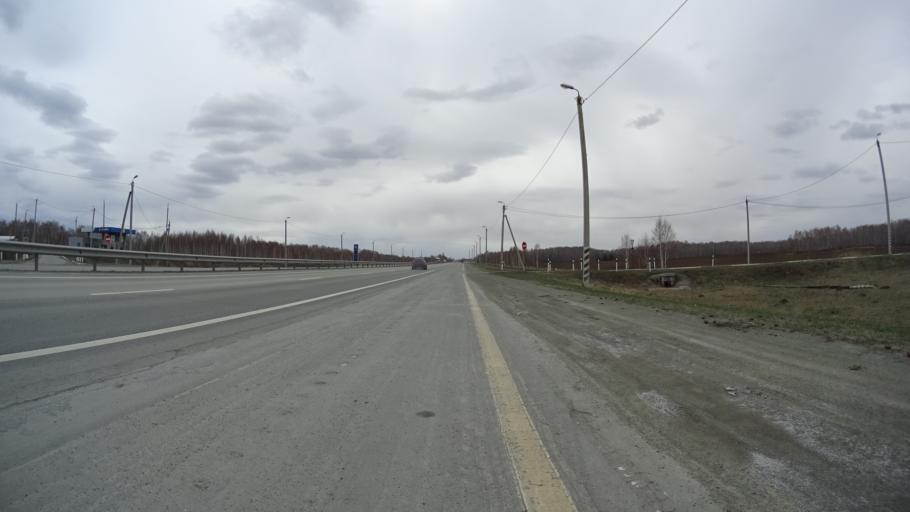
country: RU
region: Chelyabinsk
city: Yemanzhelinka
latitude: 54.8339
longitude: 61.3123
